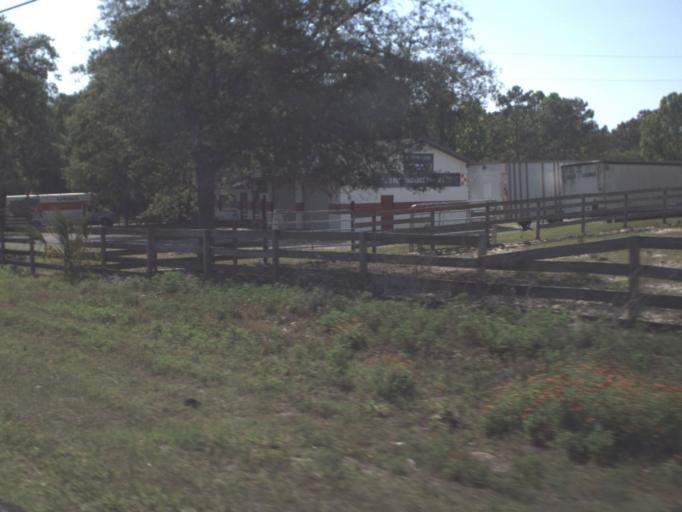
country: US
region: Florida
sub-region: Marion County
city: Dunnellon
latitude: 29.1290
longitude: -82.4121
